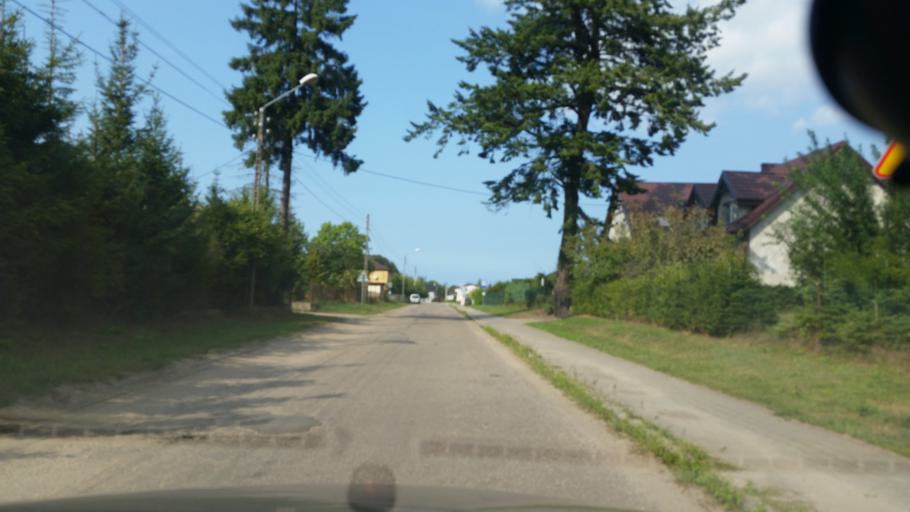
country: PL
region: Pomeranian Voivodeship
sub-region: Powiat wejherowski
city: Choczewo
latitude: 54.7685
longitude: 17.7938
